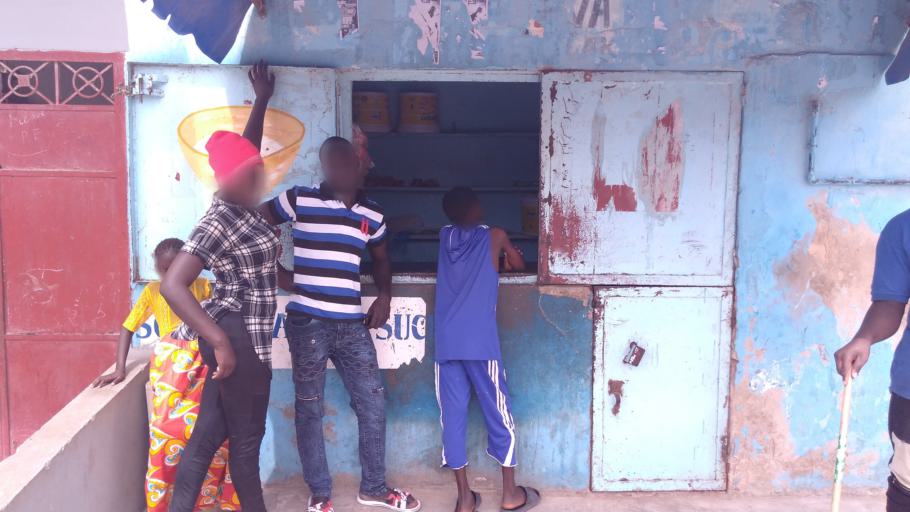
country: SN
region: Dakar
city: Pikine
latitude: 14.6888
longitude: -17.2279
